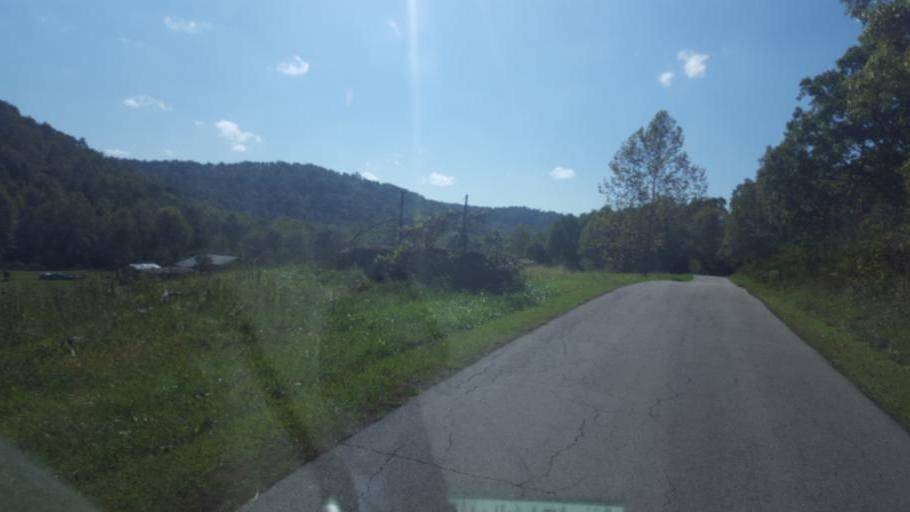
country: US
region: Kentucky
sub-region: Fleming County
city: Flemingsburg
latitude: 38.4479
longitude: -83.5497
